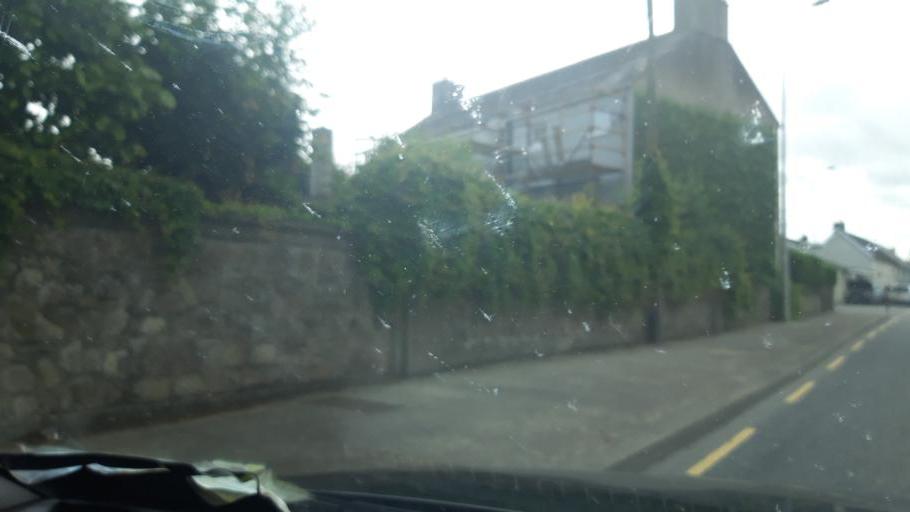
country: IE
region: Leinster
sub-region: Kilkenny
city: Callan
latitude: 52.4616
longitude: -7.4633
